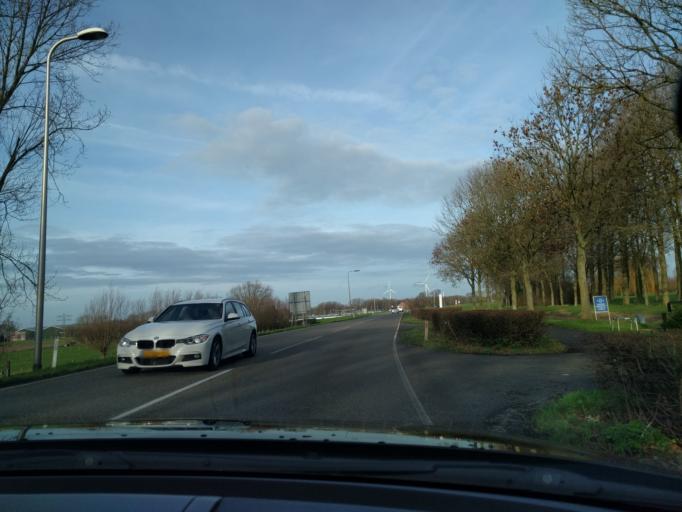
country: NL
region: South Holland
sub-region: Gemeente Maassluis
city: Maassluis
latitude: 51.8544
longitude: 4.2406
